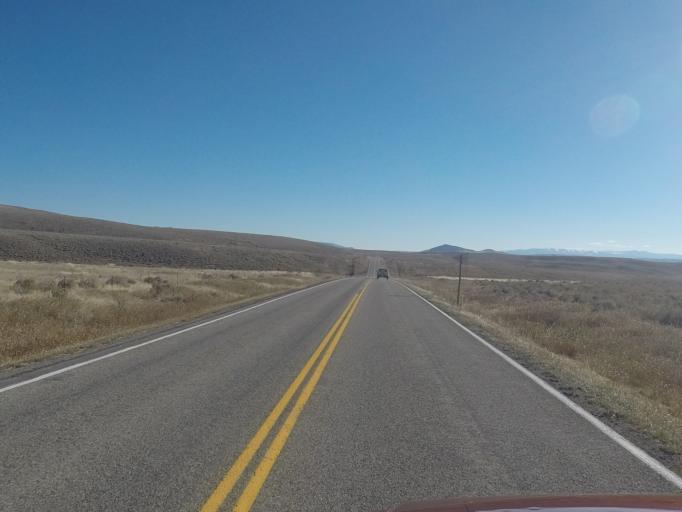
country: US
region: Montana
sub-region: Meagher County
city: White Sulphur Springs
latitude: 46.3543
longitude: -111.0366
